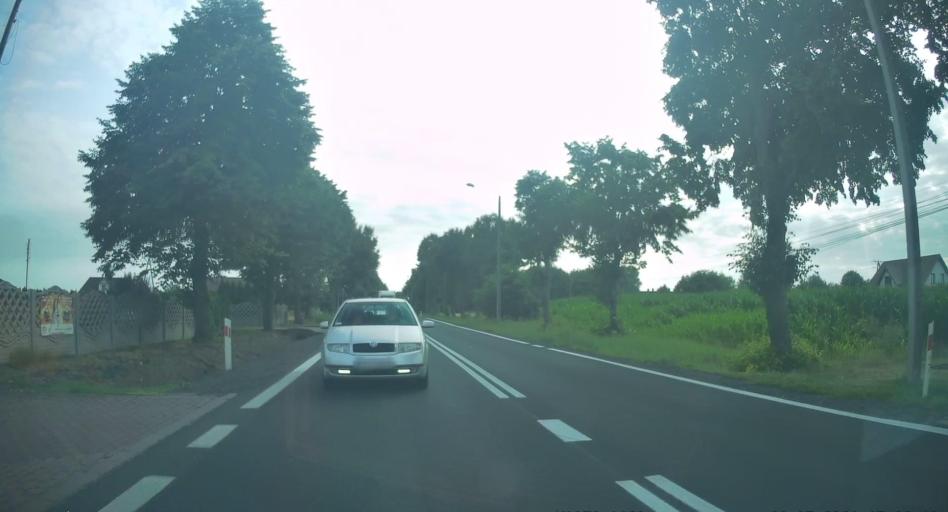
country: PL
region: Silesian Voivodeship
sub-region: Powiat czestochowski
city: Borowno
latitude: 50.9112
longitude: 19.3057
